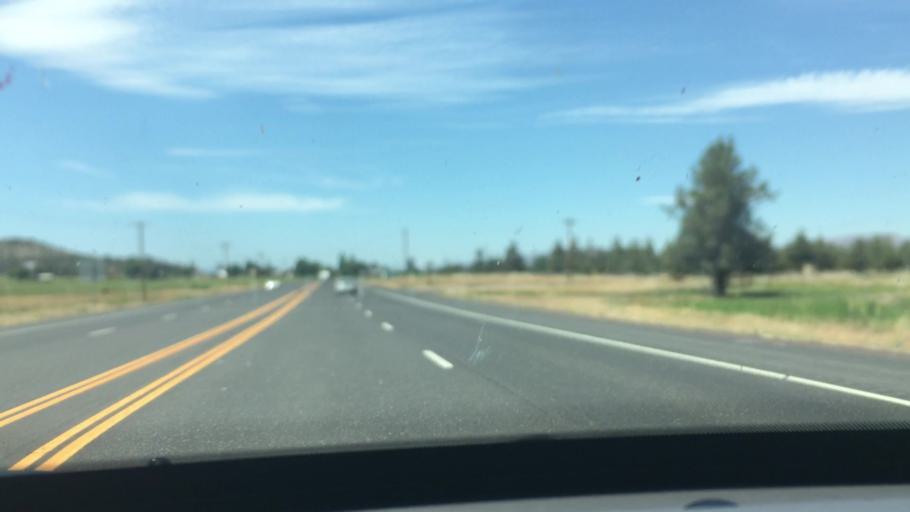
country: US
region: Oregon
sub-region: Deschutes County
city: Terrebonne
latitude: 44.3221
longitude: -121.1738
